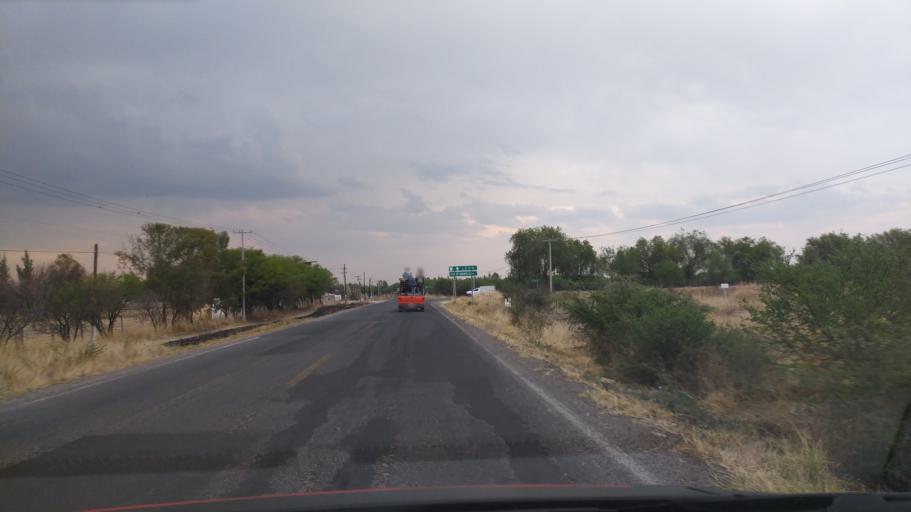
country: MX
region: Guanajuato
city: Ciudad Manuel Doblado
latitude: 20.7879
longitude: -101.9073
